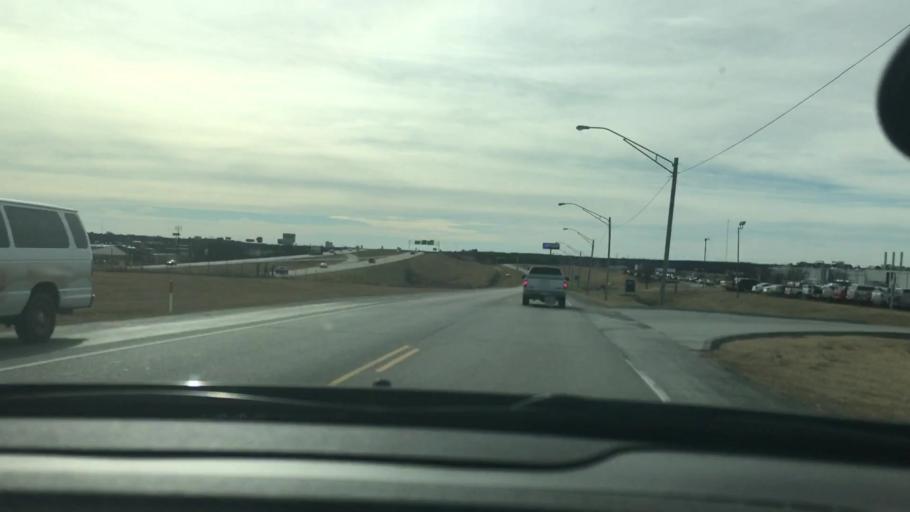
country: US
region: Oklahoma
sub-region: Carter County
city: Ardmore
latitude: 34.1836
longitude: -97.1687
